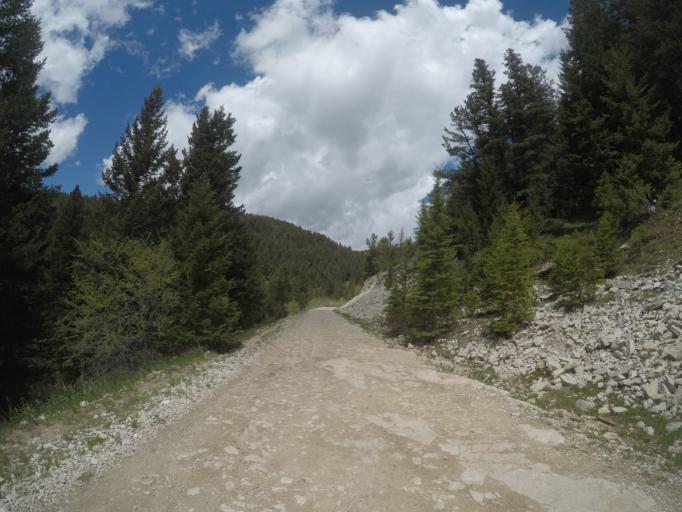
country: US
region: Wyoming
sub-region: Big Horn County
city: Lovell
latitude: 45.1685
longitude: -108.4132
